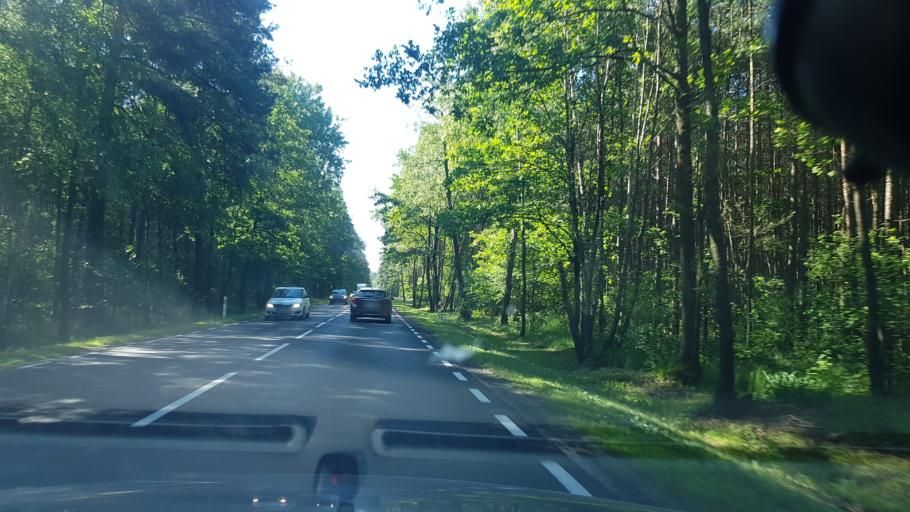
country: PL
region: Masovian Voivodeship
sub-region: Powiat wyszkowski
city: Branszczyk
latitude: 52.5754
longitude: 21.5382
